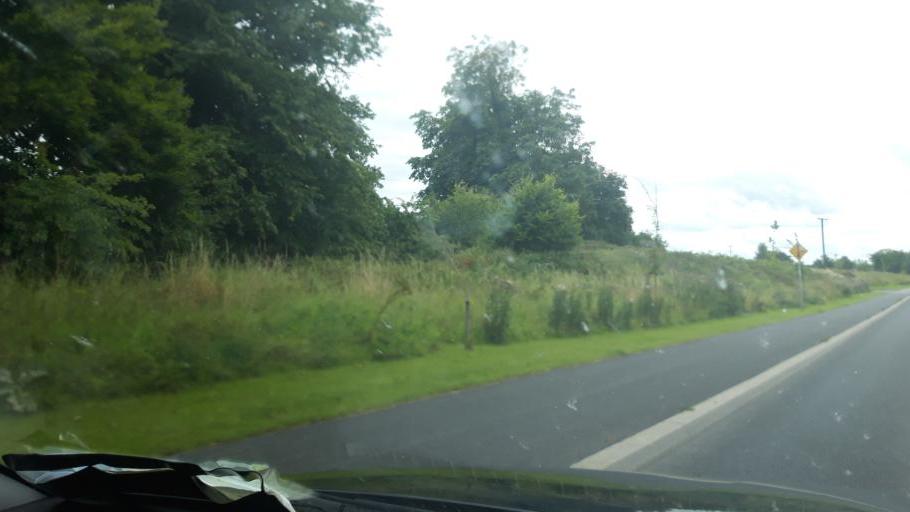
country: IE
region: Leinster
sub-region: Kilkenny
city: Kilkenny
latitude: 52.6360
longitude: -7.2723
